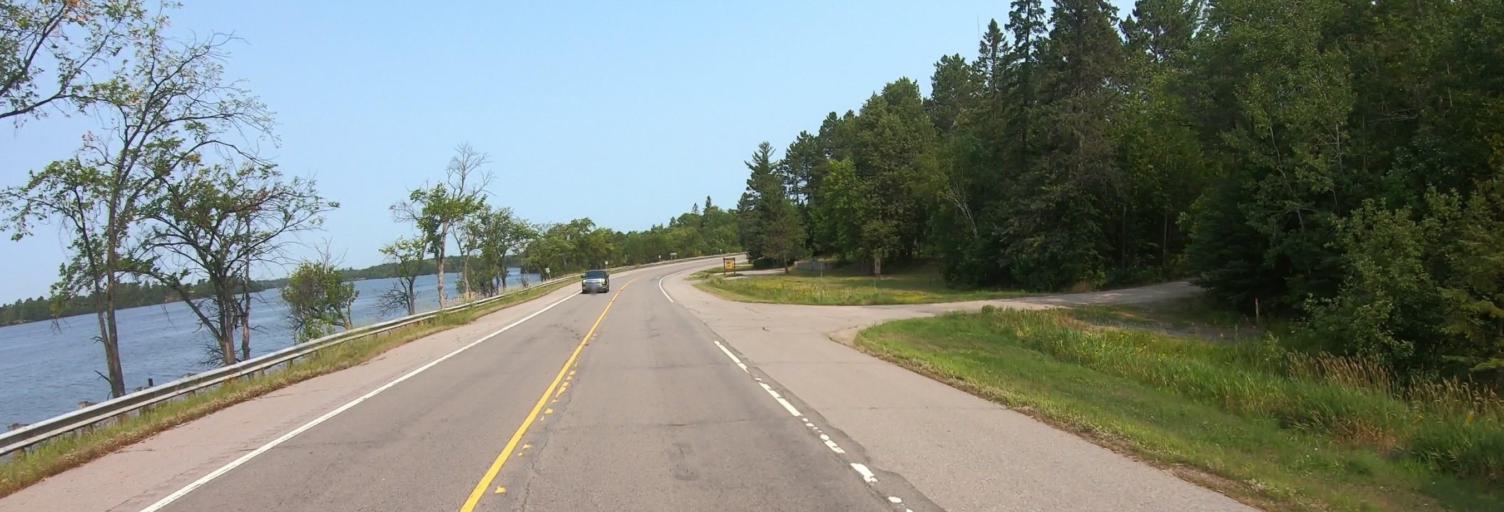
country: US
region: Minnesota
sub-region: Saint Louis County
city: Mountain Iron
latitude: 48.0599
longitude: -92.8307
